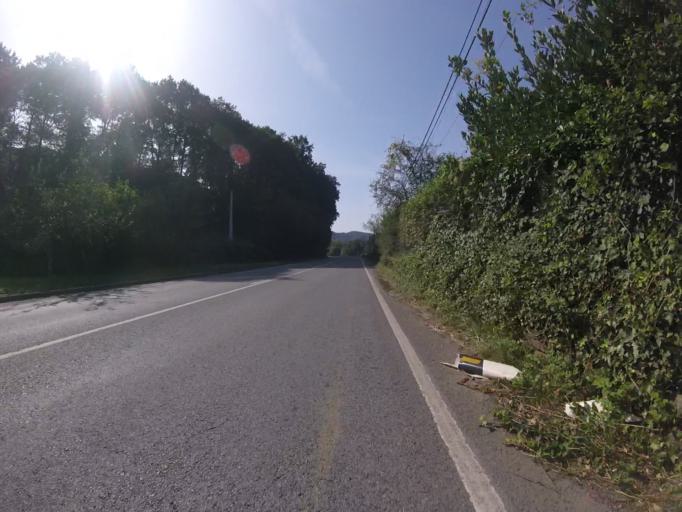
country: ES
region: Navarre
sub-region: Provincia de Navarra
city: Zugarramurdi
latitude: 43.1731
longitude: -1.4933
